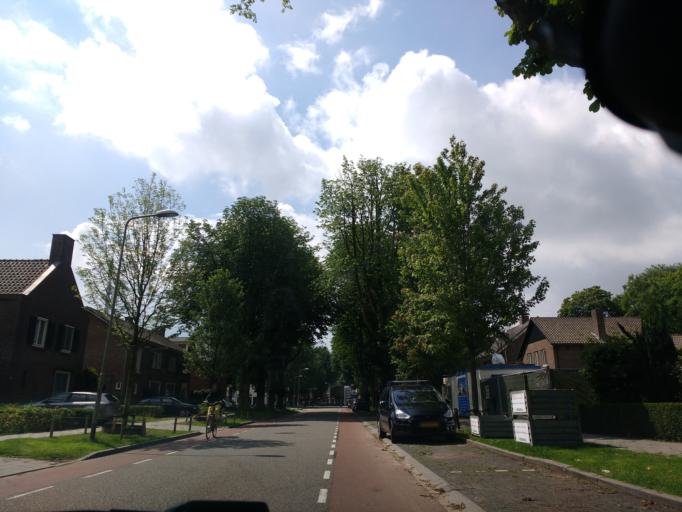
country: NL
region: Limburg
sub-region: Gemeente Venray
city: Venray
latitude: 51.5258
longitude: 5.9775
